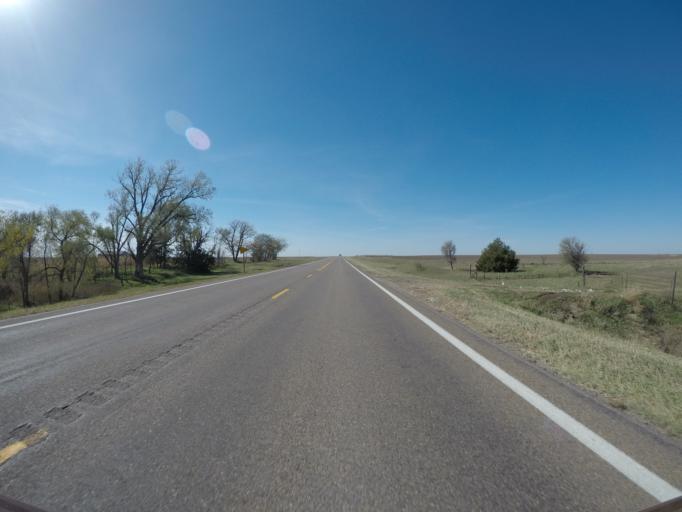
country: US
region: Kansas
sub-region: Smith County
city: Smith Center
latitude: 39.7710
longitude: -98.9443
